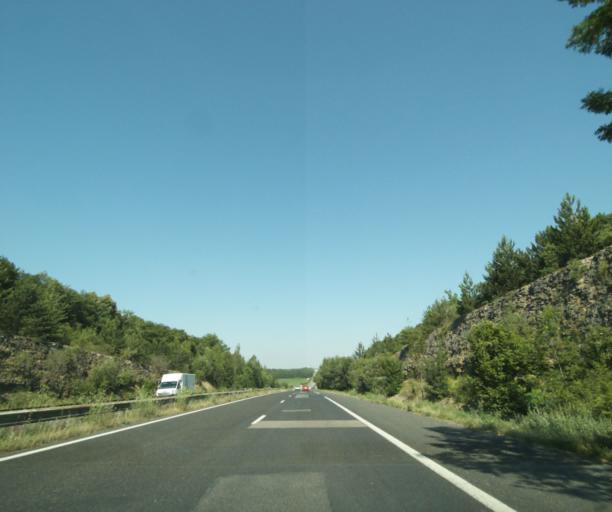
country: FR
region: Lorraine
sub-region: Departement de Meurthe-et-Moselle
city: Foug
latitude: 48.6756
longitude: 5.7651
